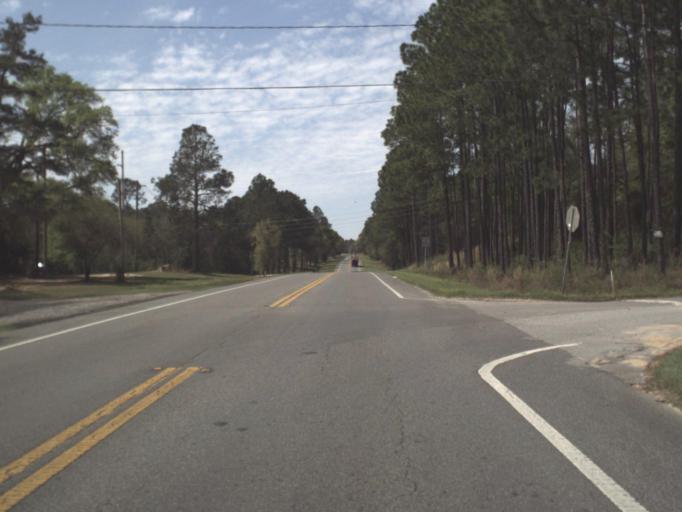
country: US
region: Florida
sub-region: Okaloosa County
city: Crestview
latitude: 30.7471
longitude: -86.6418
